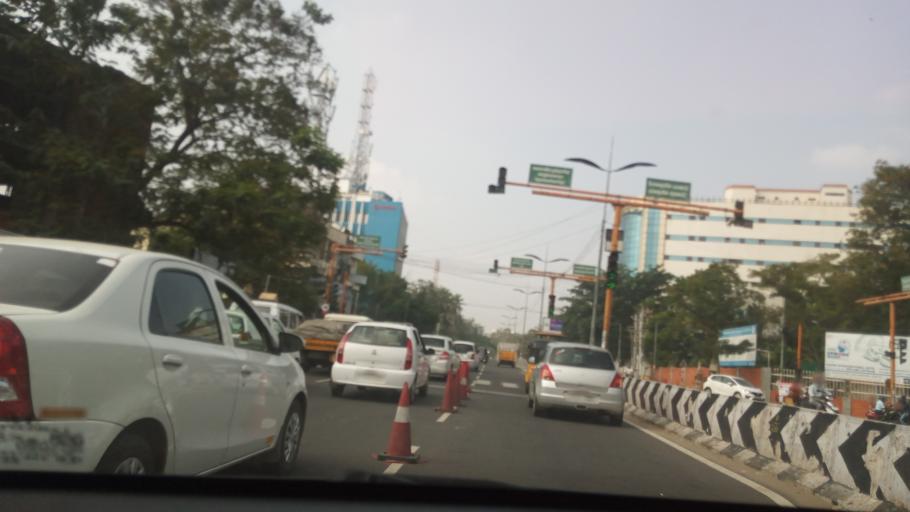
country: IN
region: Tamil Nadu
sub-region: Coimbatore
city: Coimbatore
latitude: 11.0106
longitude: 76.9824
